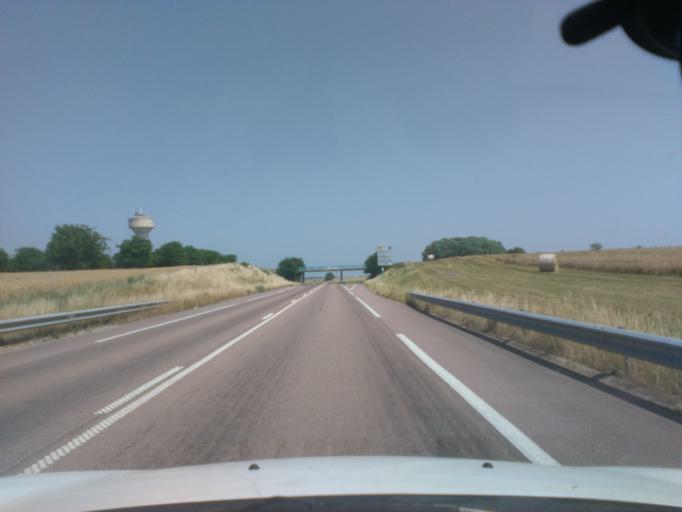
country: FR
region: Lorraine
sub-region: Departement des Vosges
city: Chatenois
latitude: 48.3054
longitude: 5.9306
